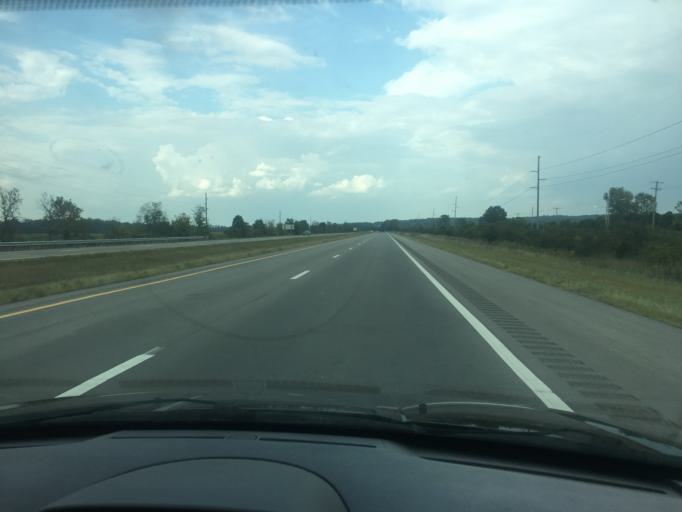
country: US
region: Ohio
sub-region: Clark County
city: Springfield
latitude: 39.9586
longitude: -83.8263
